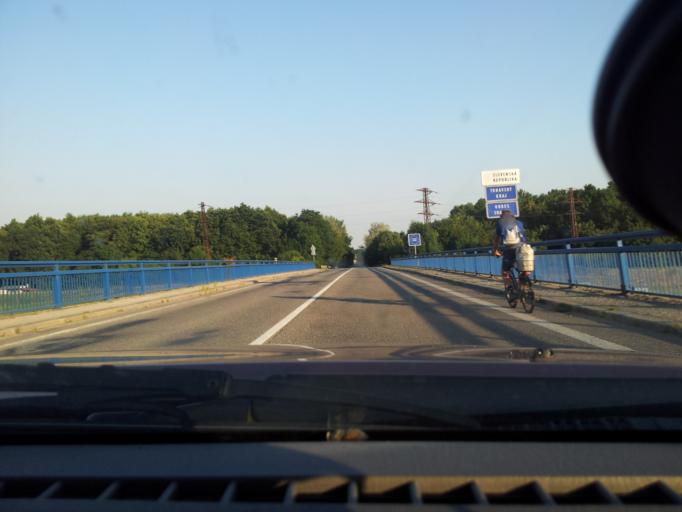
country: CZ
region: South Moravian
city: Hodonin
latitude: 48.8383
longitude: 17.1300
